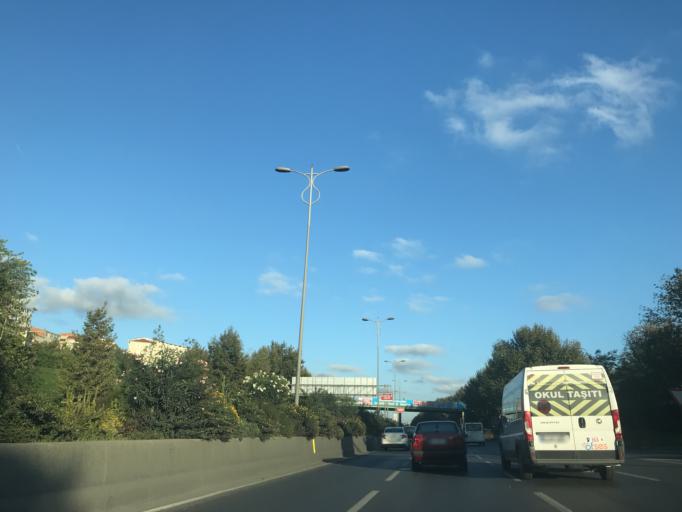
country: TR
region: Istanbul
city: Bagcilar
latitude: 41.0553
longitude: 28.8526
